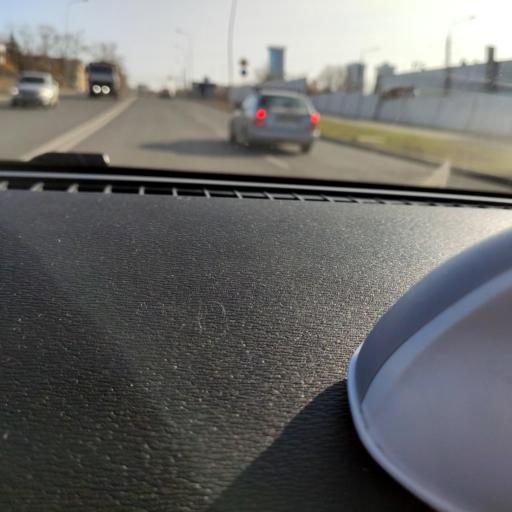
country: RU
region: Samara
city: Samara
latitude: 53.2107
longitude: 50.1505
